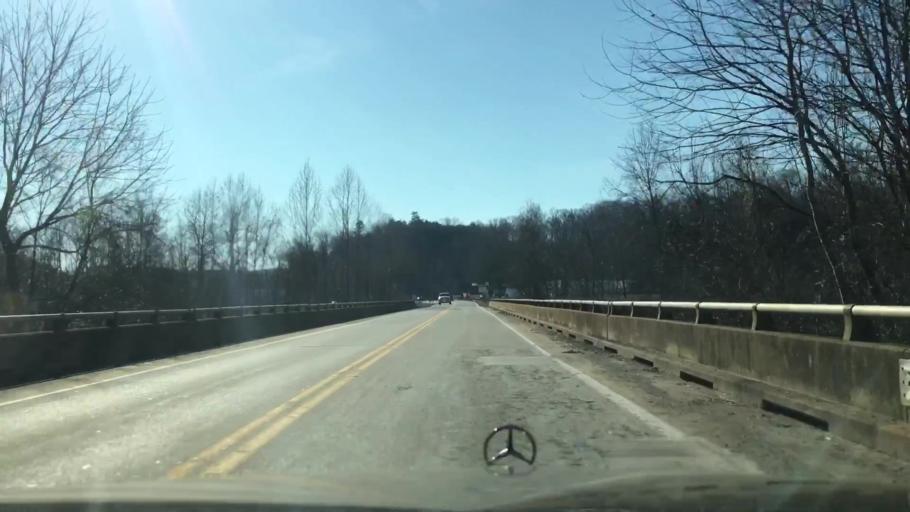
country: US
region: Virginia
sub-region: Campbell County
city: Altavista
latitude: 37.1059
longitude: -79.2858
